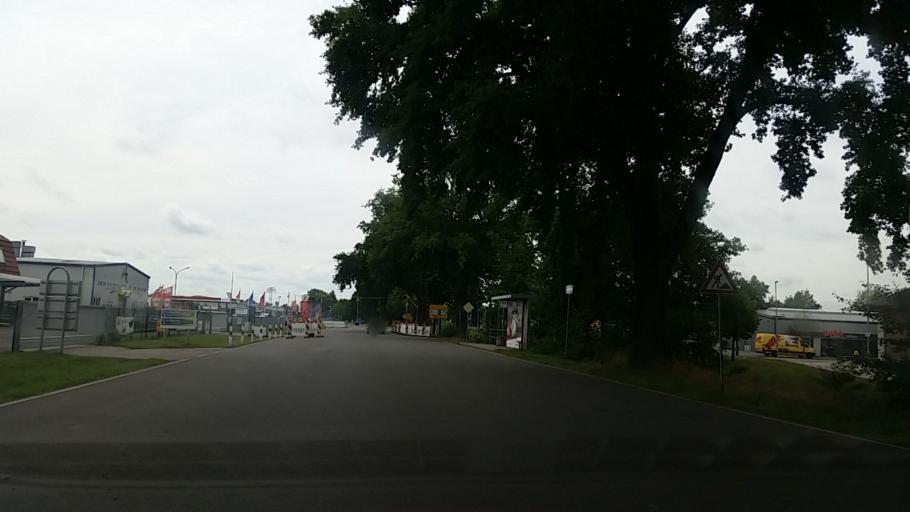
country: DE
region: Mecklenburg-Vorpommern
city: Boizenburg
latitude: 53.3811
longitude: 10.7717
